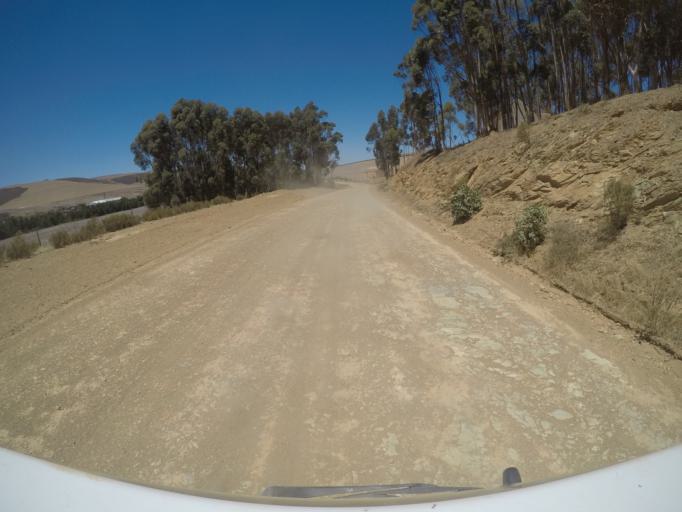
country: ZA
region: Western Cape
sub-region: Overberg District Municipality
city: Grabouw
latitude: -34.0986
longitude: 19.2014
